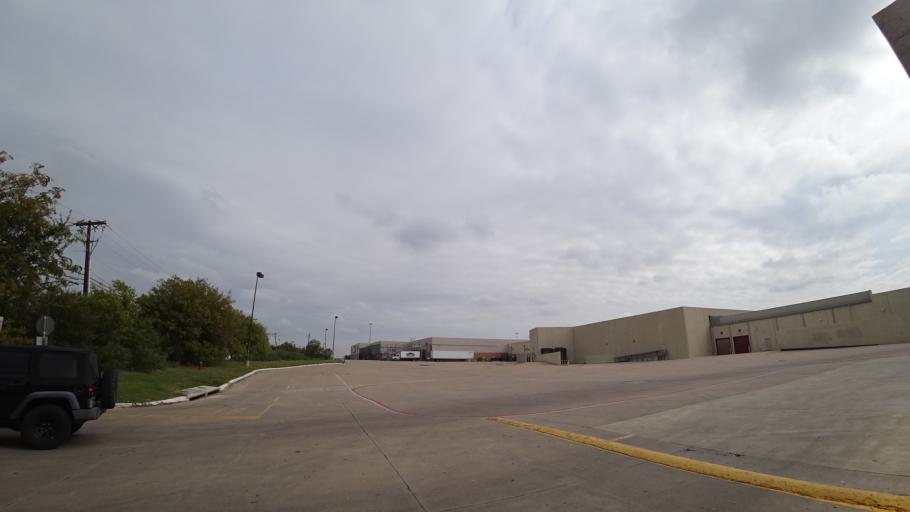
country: US
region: Texas
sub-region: Williamson County
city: Round Rock
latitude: 30.4861
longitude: -97.6801
